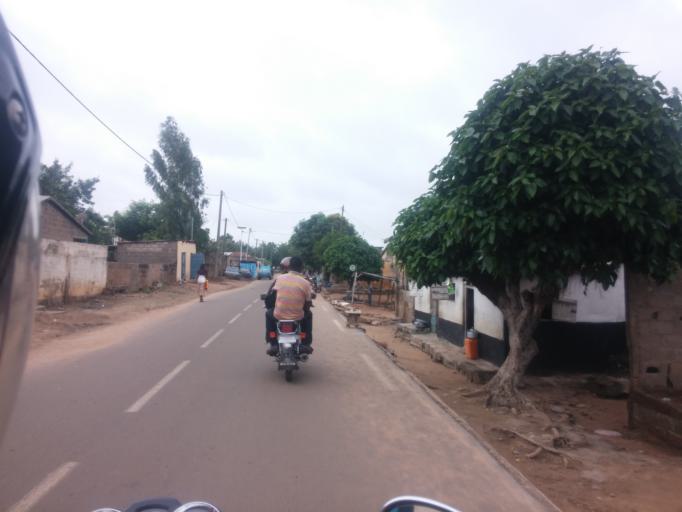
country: TG
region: Kara
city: Kara
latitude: 9.5471
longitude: 1.1886
